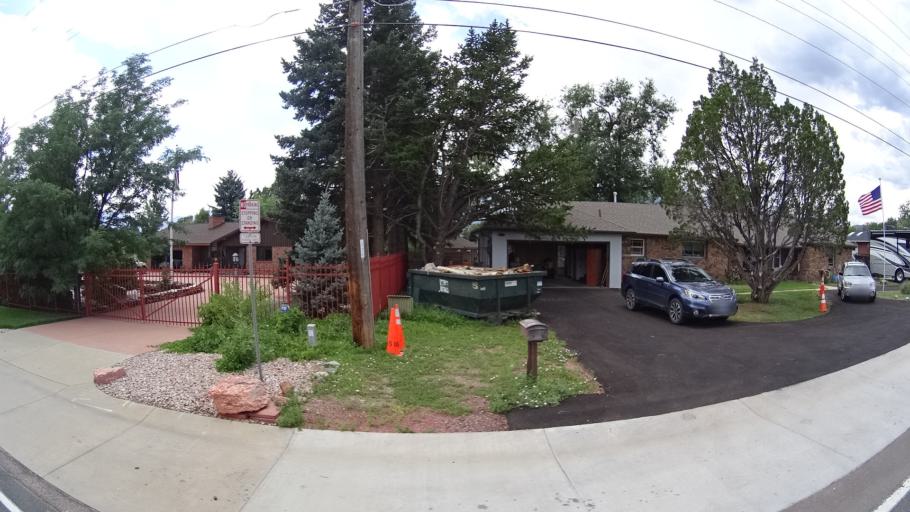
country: US
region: Colorado
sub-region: El Paso County
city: Colorado Springs
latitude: 38.8673
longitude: -104.8573
